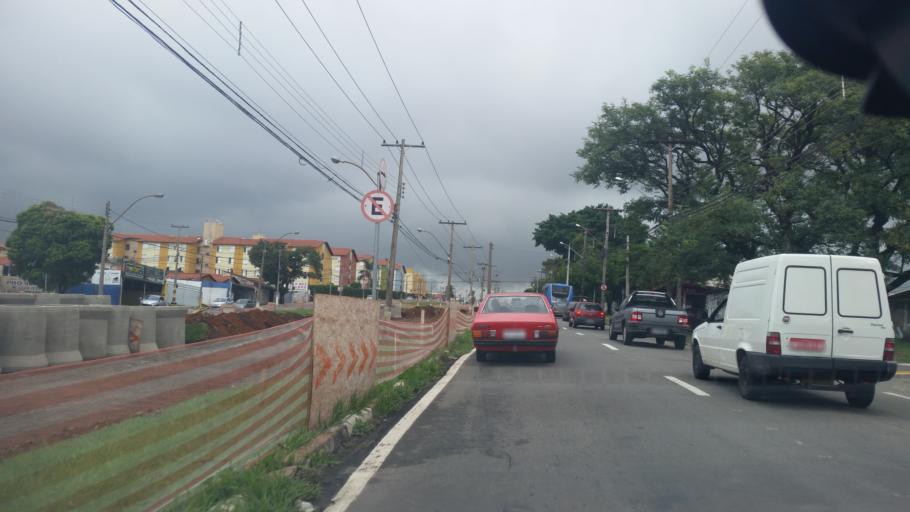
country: BR
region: Sao Paulo
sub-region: Campinas
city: Campinas
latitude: -22.9157
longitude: -47.1036
